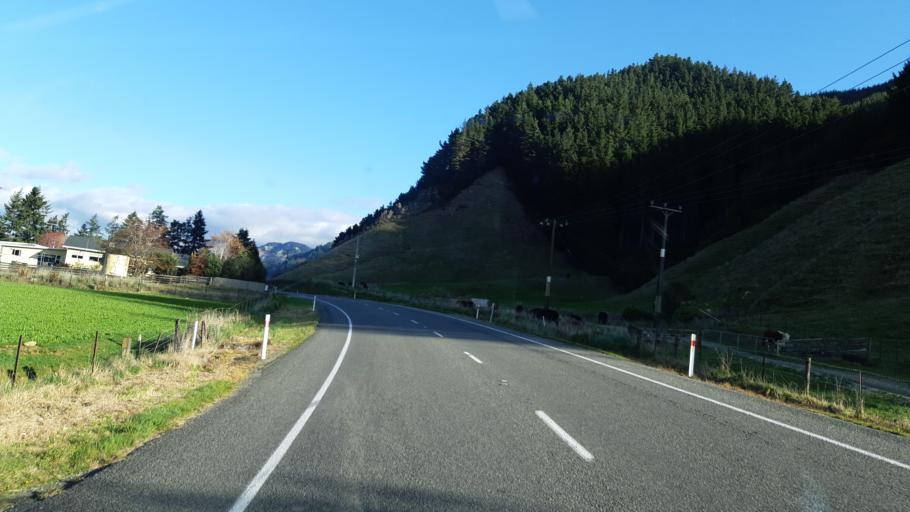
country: NZ
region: Marlborough
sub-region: Marlborough District
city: Picton
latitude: -41.3062
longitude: 173.7679
